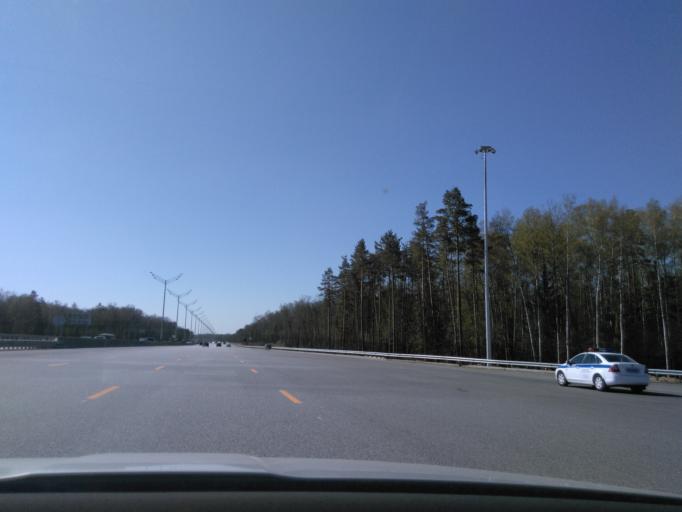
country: RU
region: Moscow
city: Khimki
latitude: 55.9335
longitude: 37.4513
